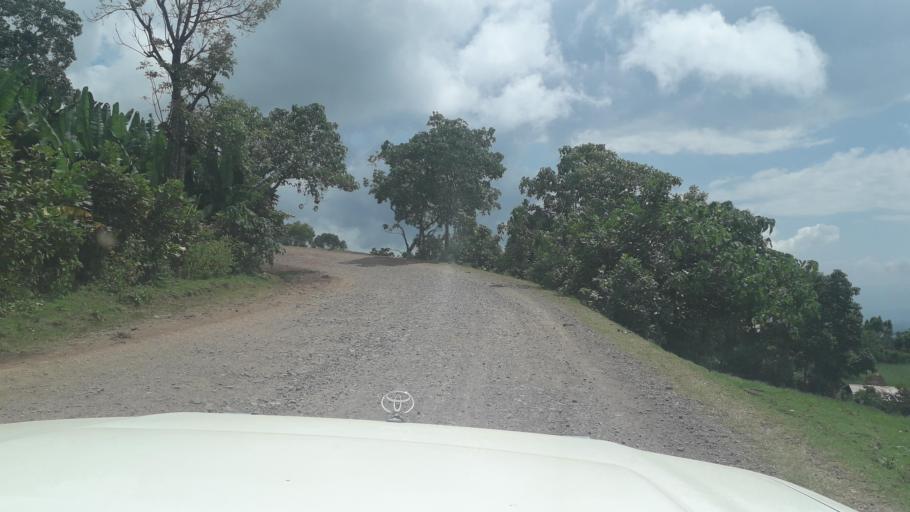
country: ET
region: Oromiya
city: Jima
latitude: 7.4301
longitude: 36.8757
